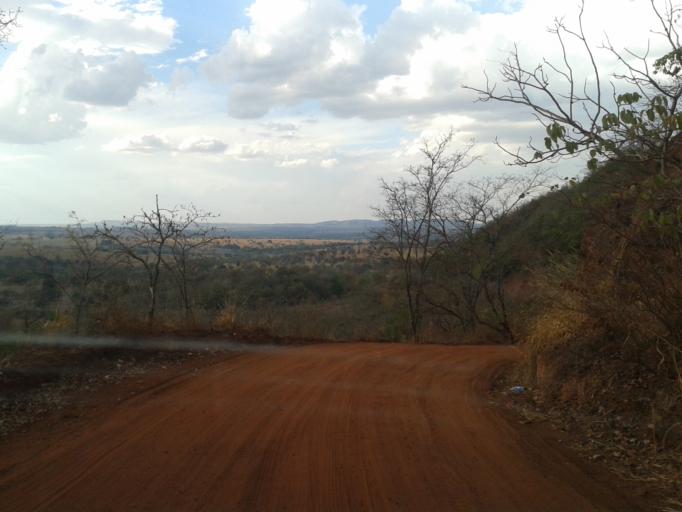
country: BR
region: Minas Gerais
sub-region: Santa Vitoria
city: Santa Vitoria
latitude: -19.1835
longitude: -49.8589
